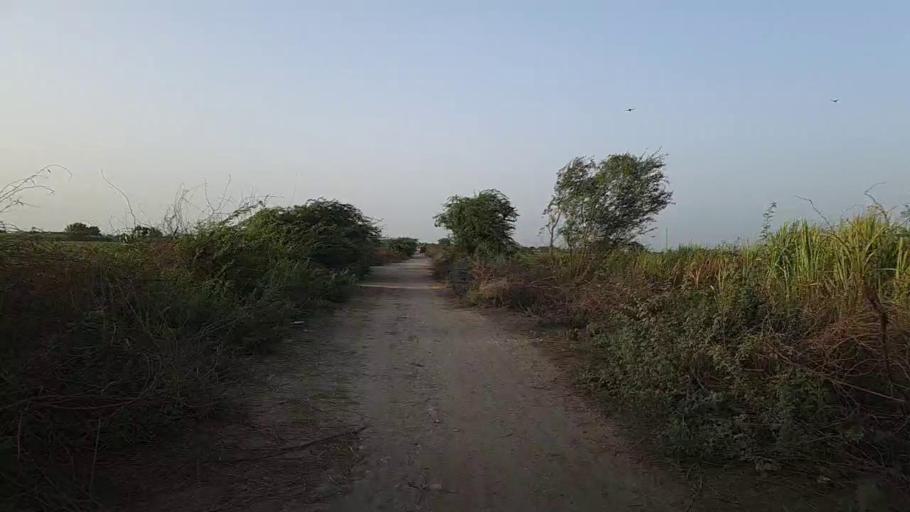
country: PK
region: Sindh
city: Kario
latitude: 24.7095
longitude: 68.4621
